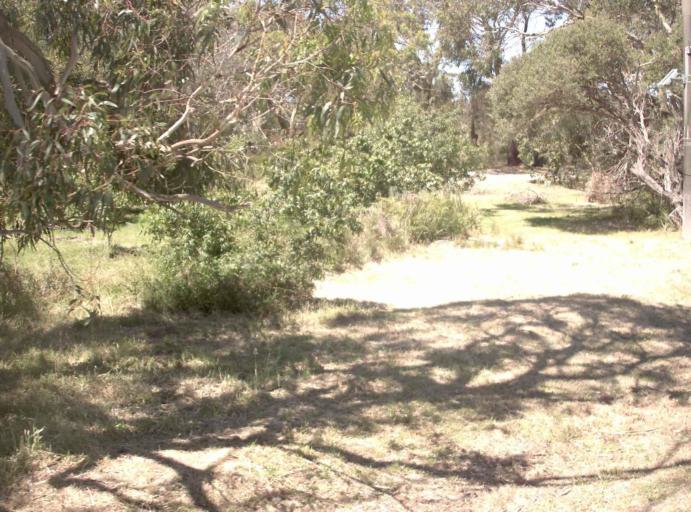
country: AU
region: Victoria
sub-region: Bass Coast
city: North Wonthaggi
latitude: -38.8205
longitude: 146.1210
